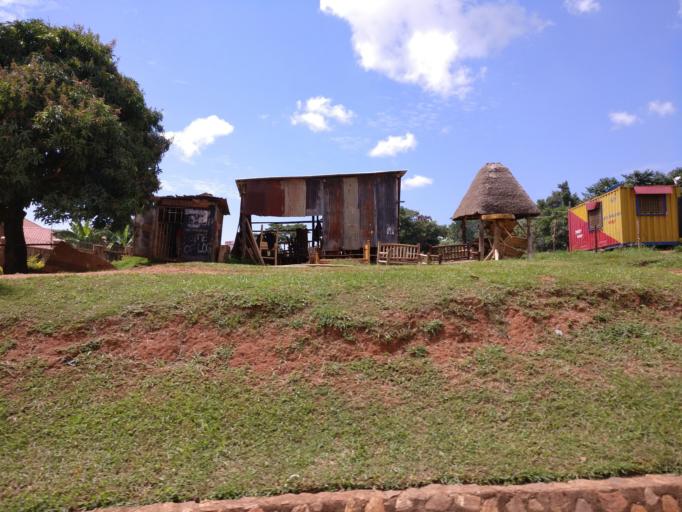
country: UG
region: Central Region
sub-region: Wakiso District
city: Kajansi
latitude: 0.1801
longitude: 32.5382
